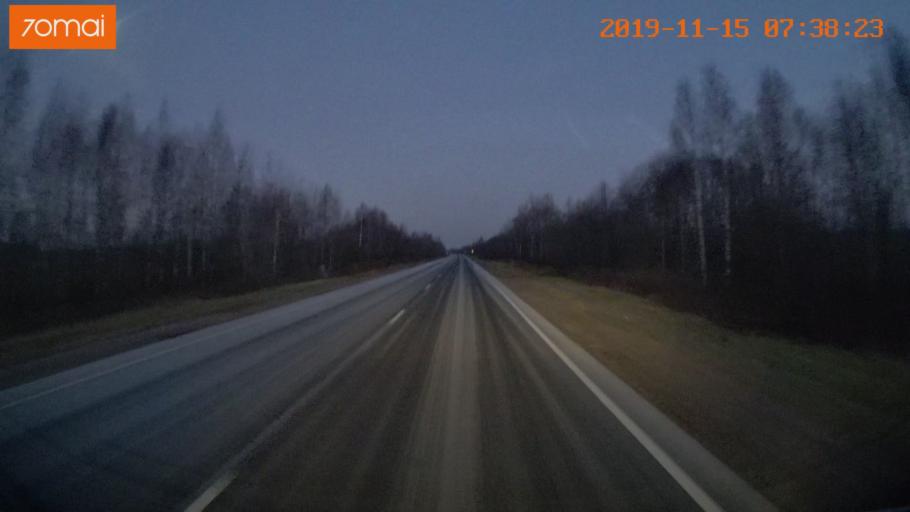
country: RU
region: Vologda
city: Sheksna
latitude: 58.7567
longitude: 38.4021
